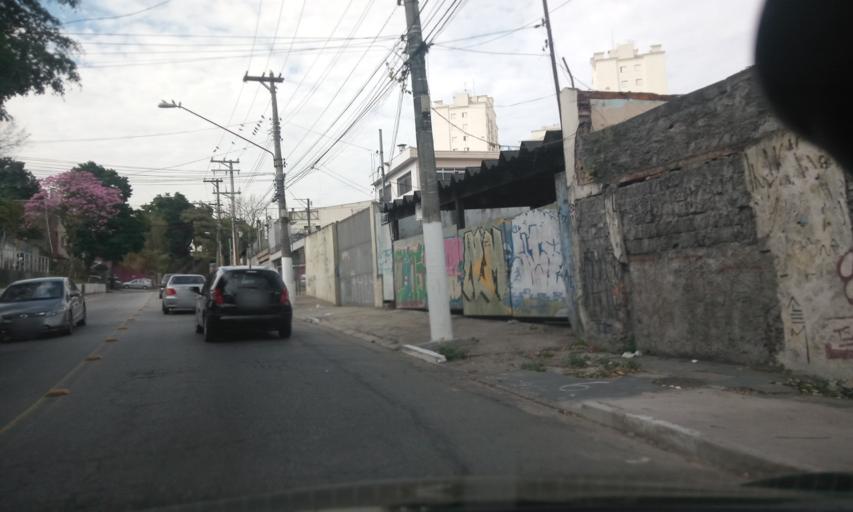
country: BR
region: Sao Paulo
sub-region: Sao Caetano Do Sul
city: Sao Caetano do Sul
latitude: -23.6134
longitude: -46.6064
